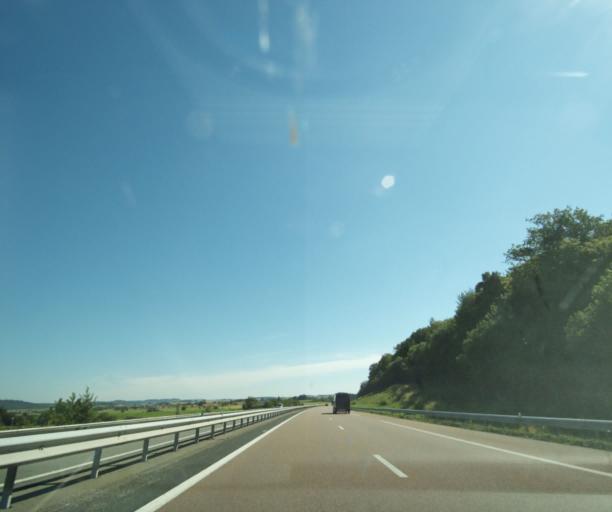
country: FR
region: Champagne-Ardenne
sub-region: Departement de la Haute-Marne
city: Saulxures
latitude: 48.0732
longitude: 5.5989
